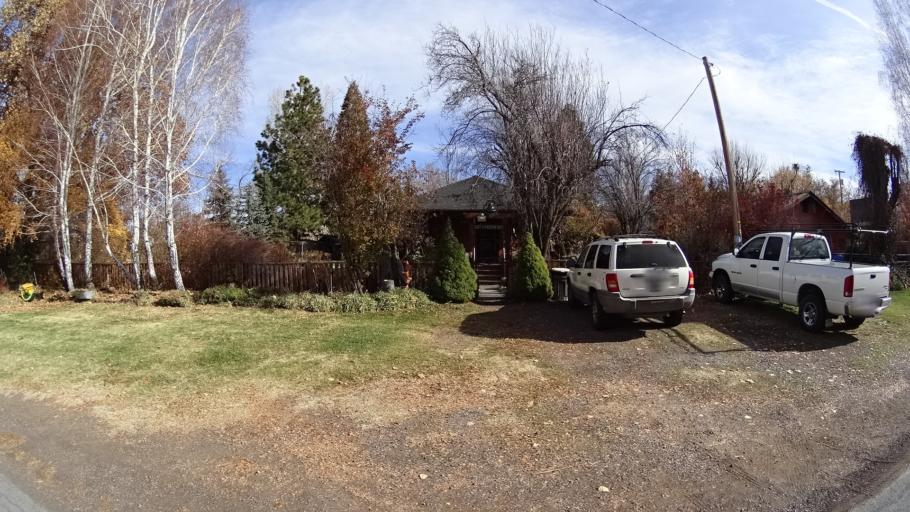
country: US
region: California
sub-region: Siskiyou County
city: Weed
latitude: 41.4599
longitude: -122.4330
